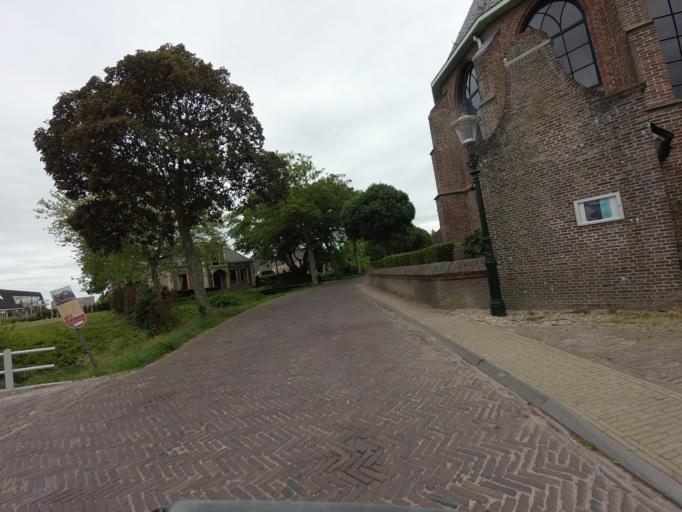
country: NL
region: North Holland
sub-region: Gemeente Medemblik
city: Opperdoes
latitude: 52.7438
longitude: 5.0606
